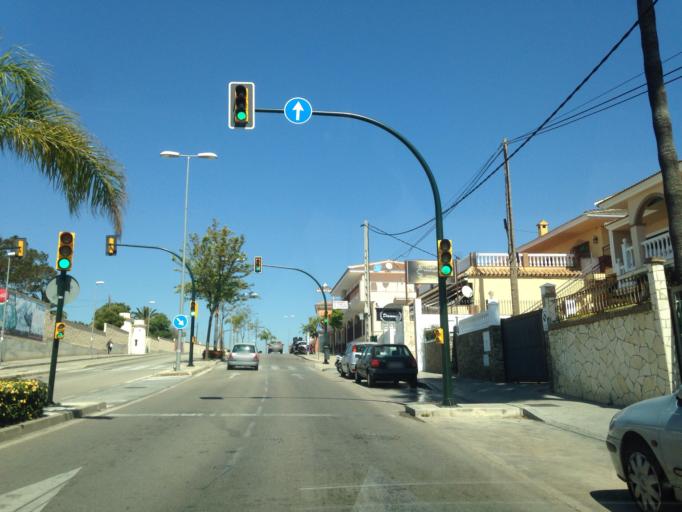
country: ES
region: Andalusia
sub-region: Provincia de Malaga
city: Malaga
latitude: 36.7463
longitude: -4.4920
